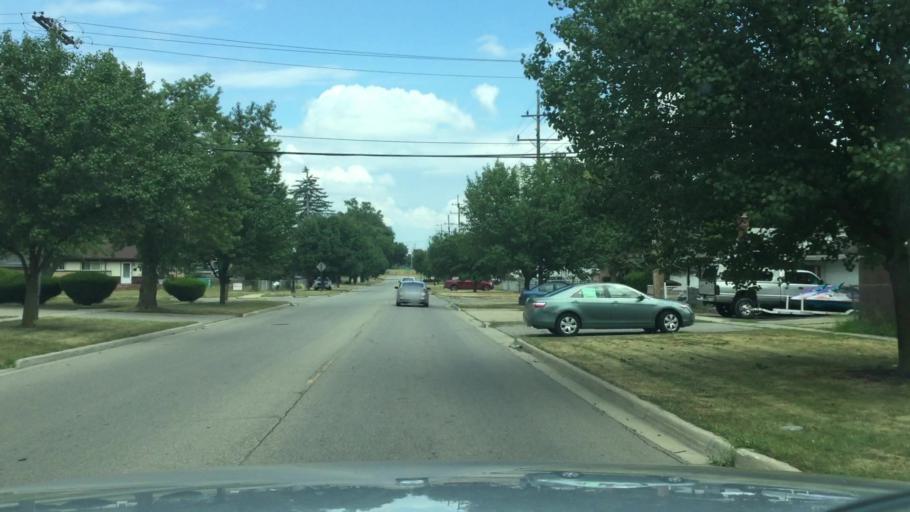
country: US
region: Michigan
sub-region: Washtenaw County
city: Ypsilanti
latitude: 42.2318
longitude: -83.5683
